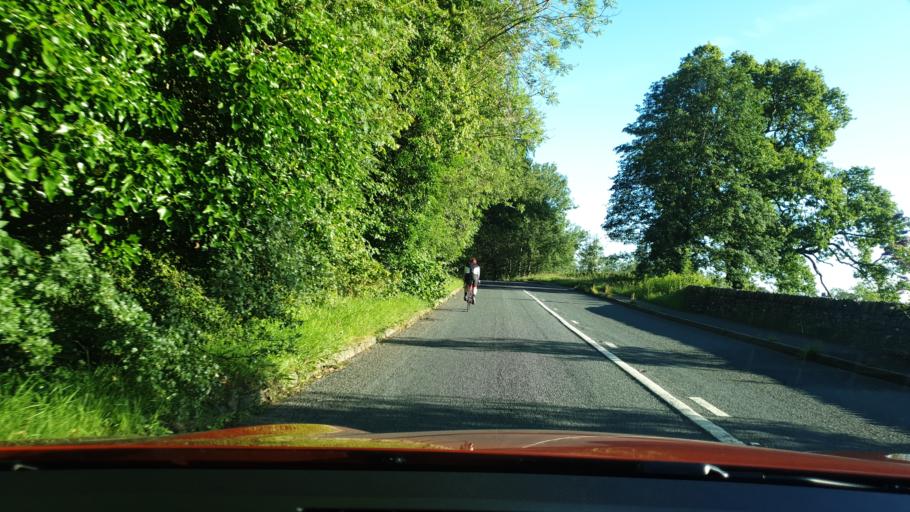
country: GB
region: England
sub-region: Cumbria
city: Windermere
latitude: 54.4047
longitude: -2.9108
